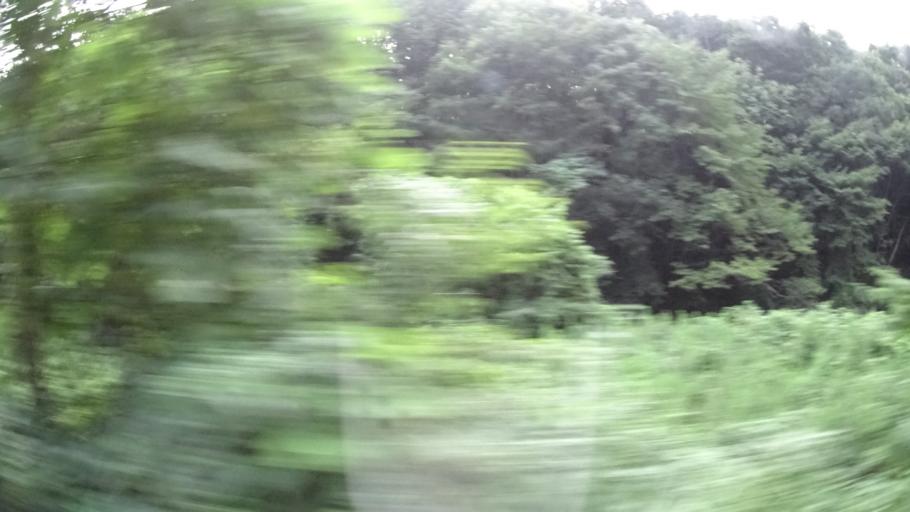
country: JP
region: Tochigi
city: Karasuyama
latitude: 36.6130
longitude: 140.1545
